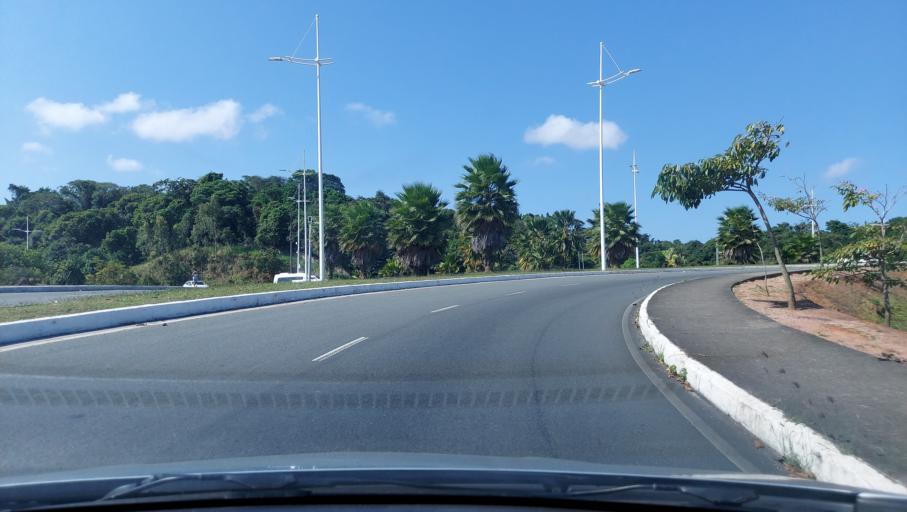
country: BR
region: Bahia
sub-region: Salvador
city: Salvador
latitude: -12.9733
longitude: -38.4515
